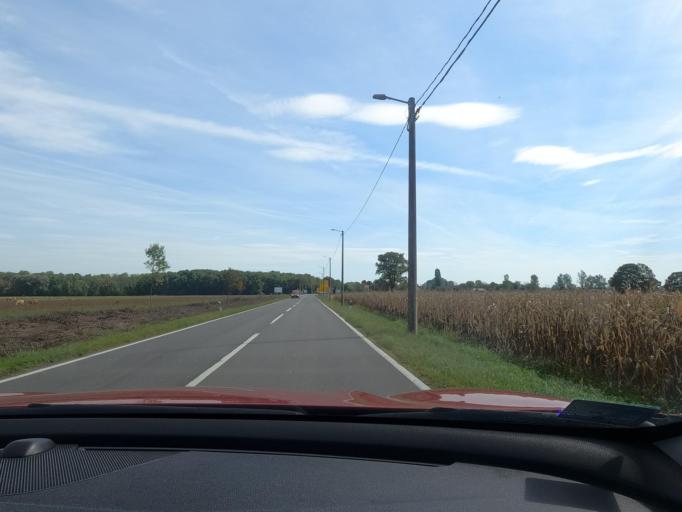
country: HR
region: Sisacko-Moslavacka
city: Budasevo
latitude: 45.4867
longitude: 16.4632
